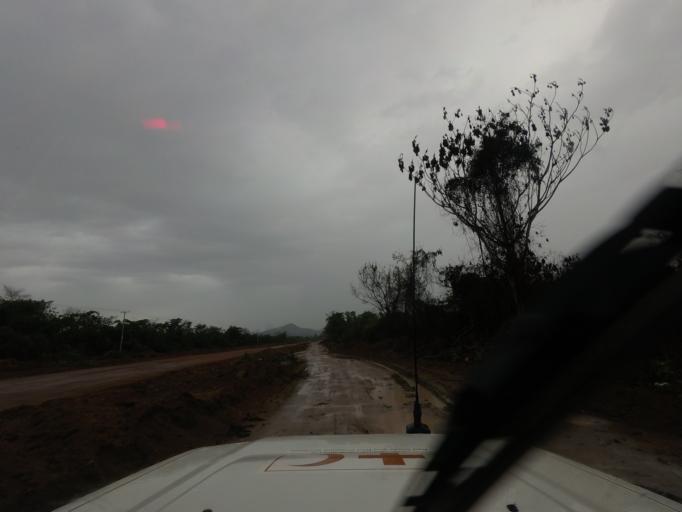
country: LR
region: Nimba
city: Sanniquellie
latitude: 7.2524
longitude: -8.8572
